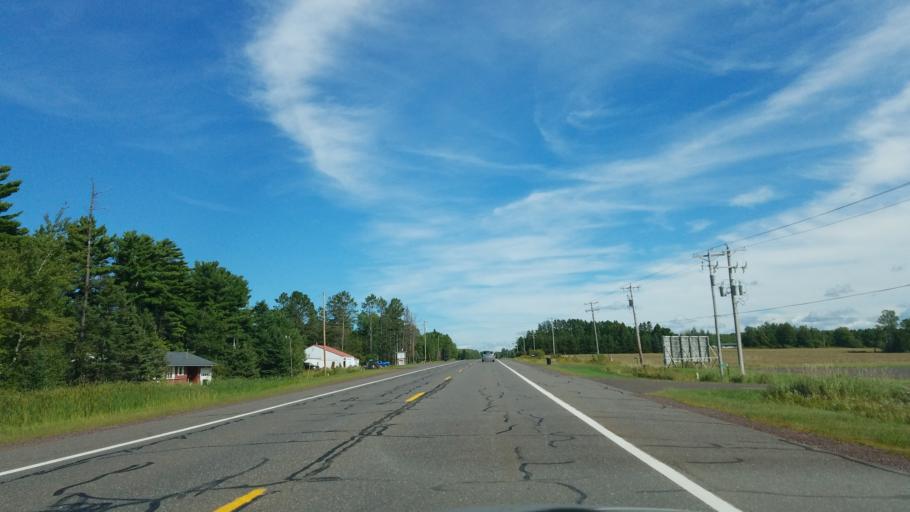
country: US
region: Michigan
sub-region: Ontonagon County
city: Ontonagon
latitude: 46.5348
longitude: -89.1643
